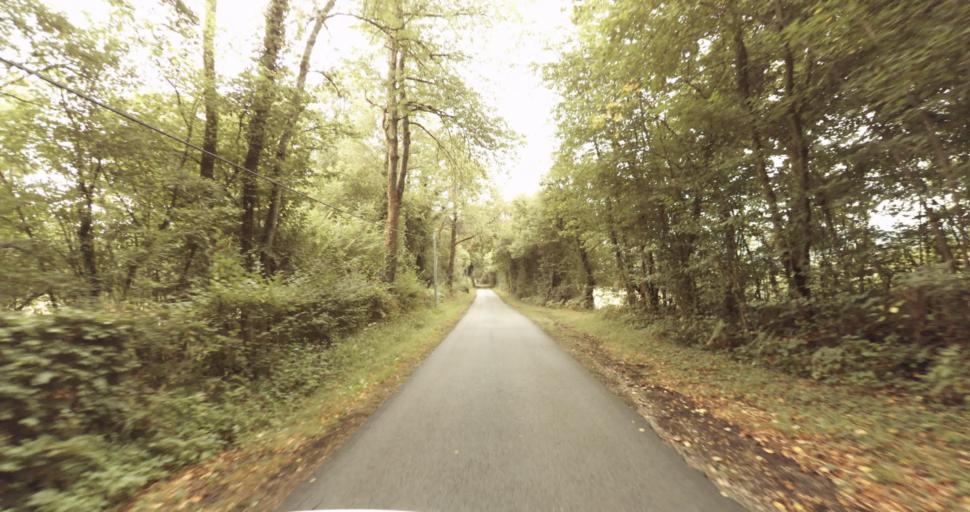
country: FR
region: Lower Normandy
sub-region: Departement de l'Orne
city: Trun
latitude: 48.9279
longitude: 0.0723
